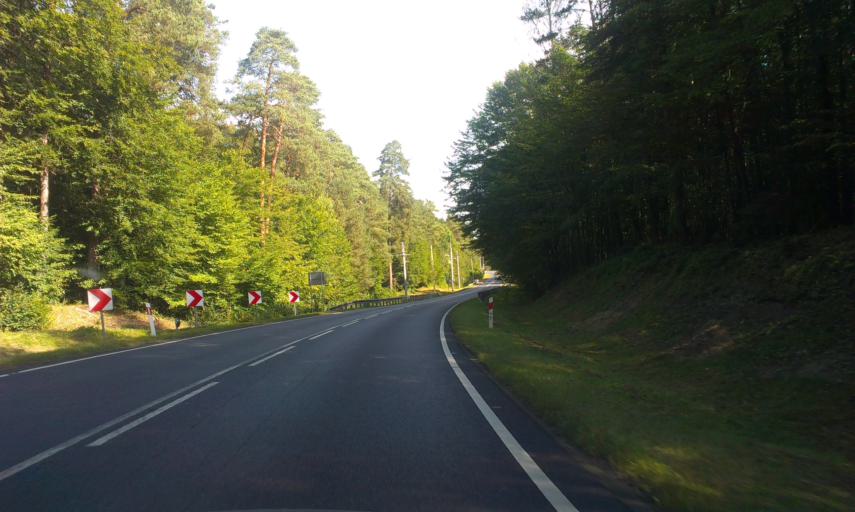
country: PL
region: Greater Poland Voivodeship
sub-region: Powiat zlotowski
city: Okonek
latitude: 53.5322
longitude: 16.9435
